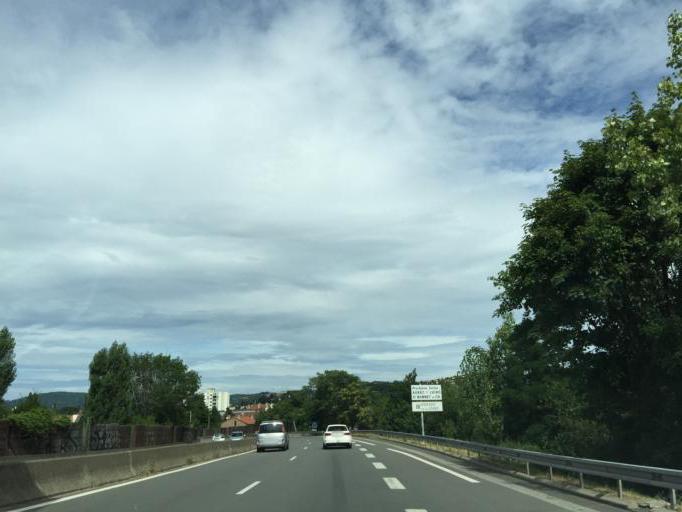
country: FR
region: Rhone-Alpes
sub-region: Departement de la Loire
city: Firminy
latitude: 45.3911
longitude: 4.2978
